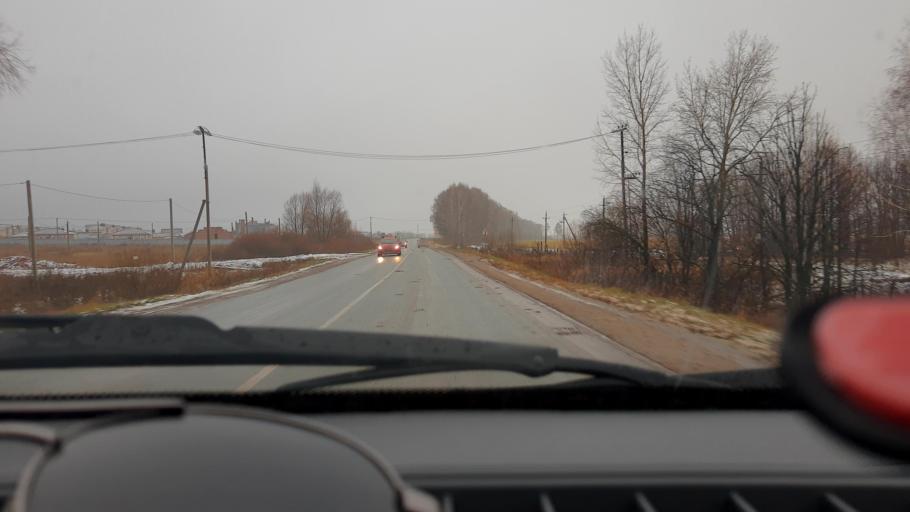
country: RU
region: Bashkortostan
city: Kabakovo
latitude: 54.5964
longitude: 56.2166
